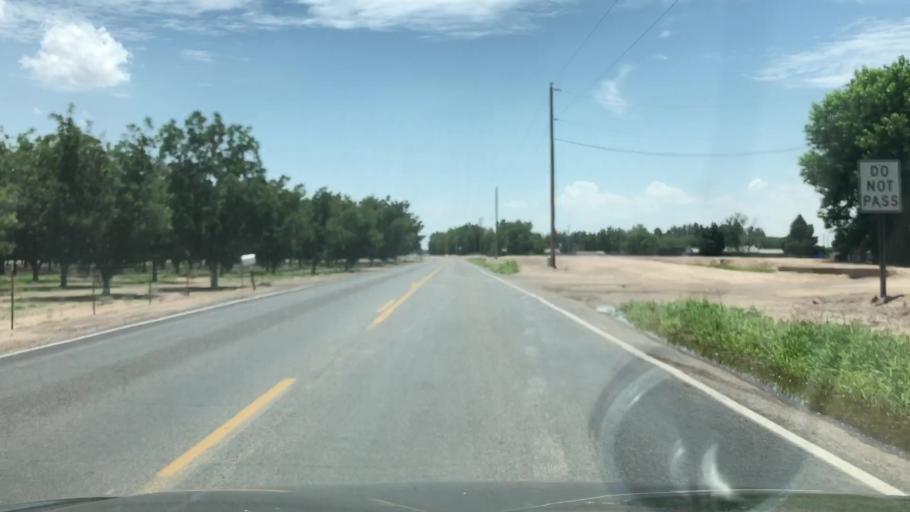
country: US
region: New Mexico
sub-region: Dona Ana County
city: La Union
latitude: 32.0079
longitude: -106.6635
